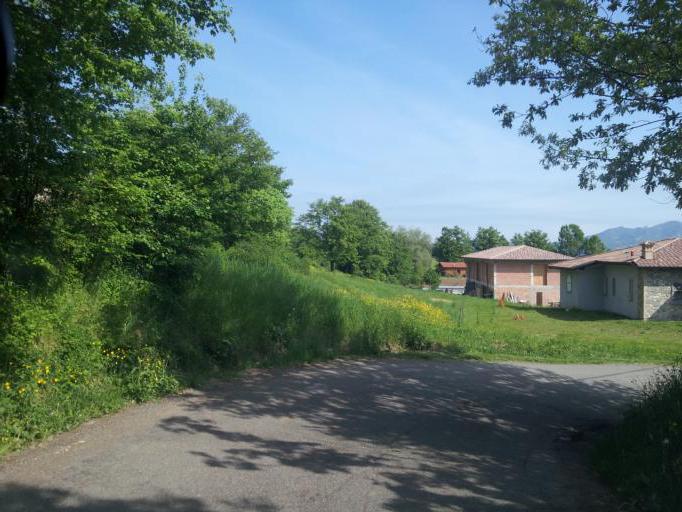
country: IT
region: Emilia-Romagna
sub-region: Provincia di Reggio Emilia
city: Villa Minozzo
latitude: 44.3671
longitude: 10.4710
